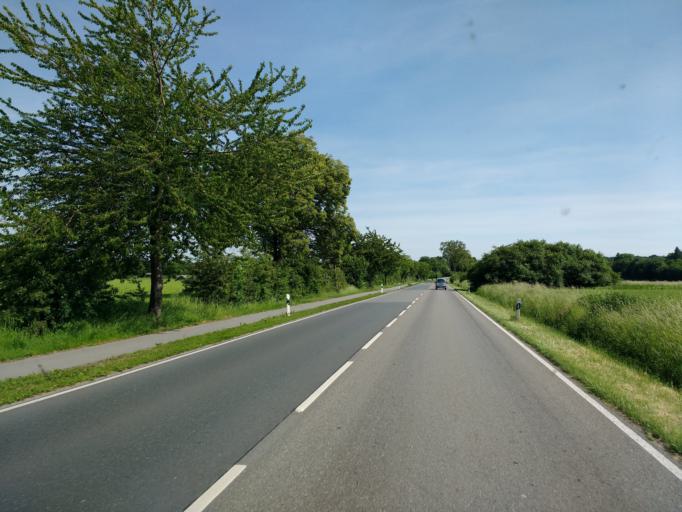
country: DE
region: North Rhine-Westphalia
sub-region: Regierungsbezirk Detmold
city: Bad Salzuflen
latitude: 52.0718
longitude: 8.7347
